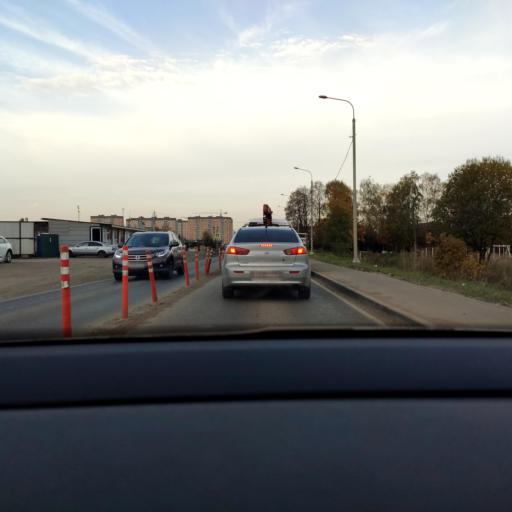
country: RU
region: Moskovskaya
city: Pirogovskiy
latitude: 55.9698
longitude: 37.7538
